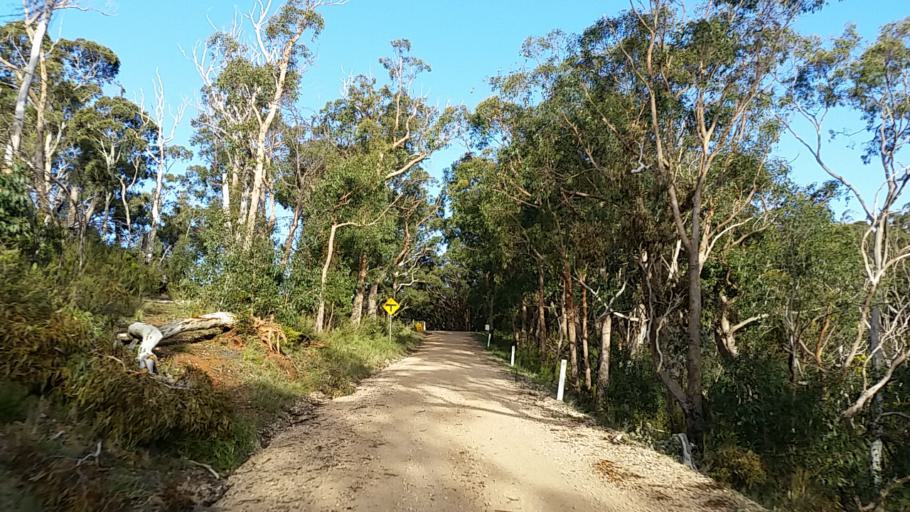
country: AU
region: South Australia
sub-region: Adelaide Hills
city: Balhannah
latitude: -34.9274
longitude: 138.7927
